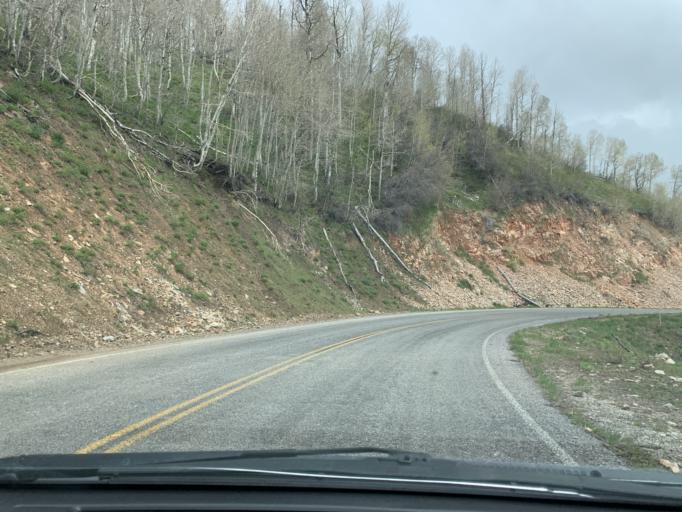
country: US
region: Utah
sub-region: Utah County
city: Elk Ridge
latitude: 39.8719
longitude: -111.6862
